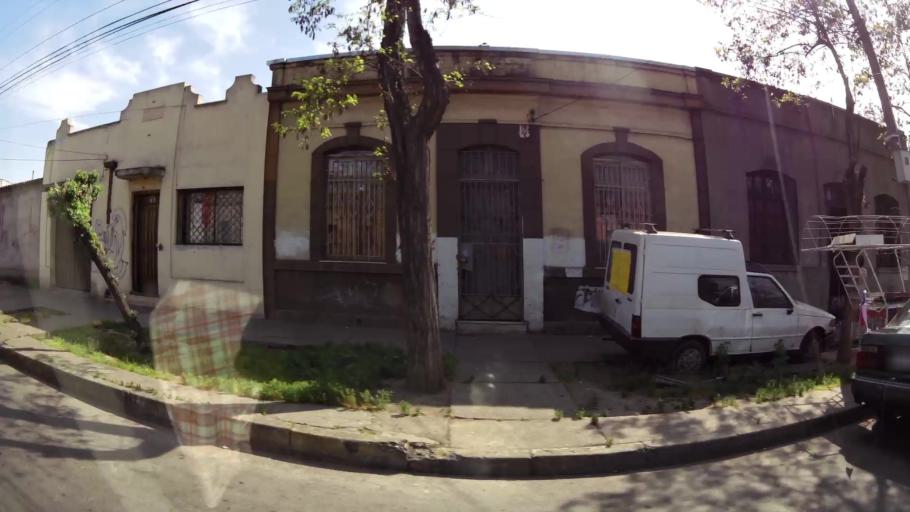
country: CL
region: Santiago Metropolitan
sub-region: Provincia de Santiago
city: Santiago
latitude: -33.4062
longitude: -70.6355
